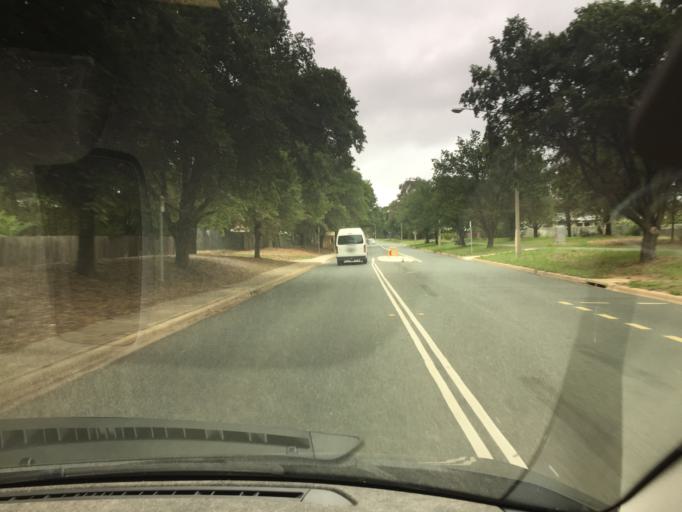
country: AU
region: Australian Capital Territory
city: Kaleen
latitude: -35.2305
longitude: 149.1125
